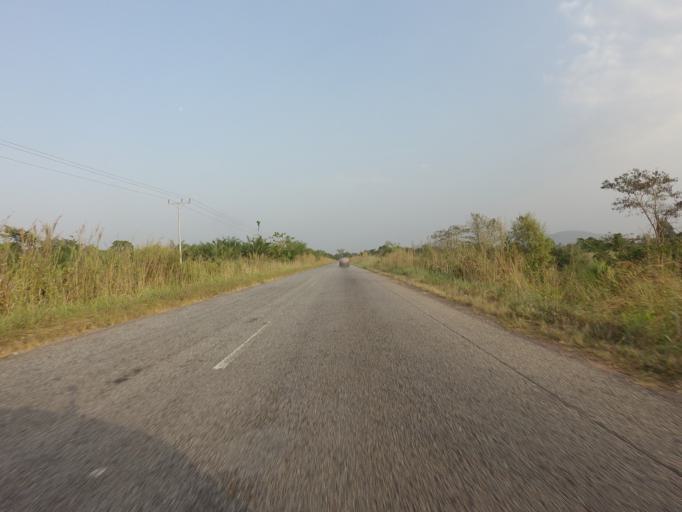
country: GH
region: Volta
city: Ho
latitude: 6.5746
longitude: 0.3397
